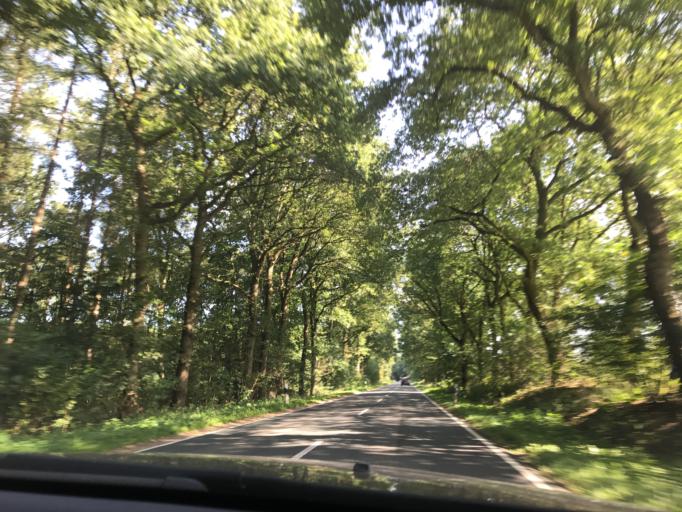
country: DE
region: Lower Saxony
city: Sogel
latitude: 52.8195
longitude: 7.4953
